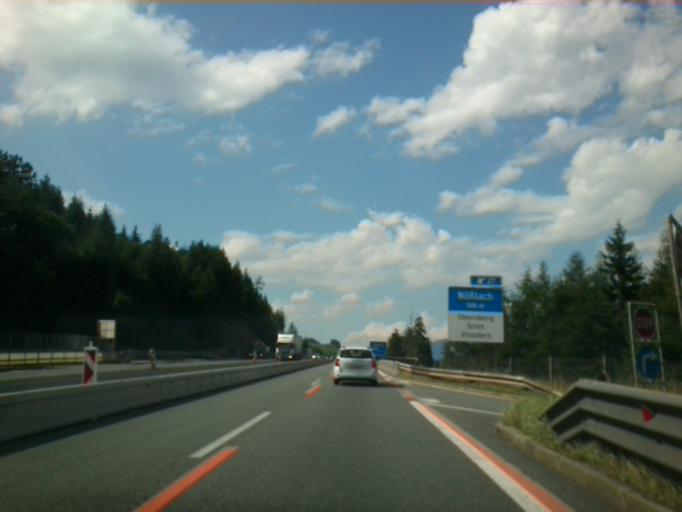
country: AT
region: Tyrol
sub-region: Politischer Bezirk Innsbruck Land
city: Gries am Brenner
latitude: 47.0527
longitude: 11.4817
